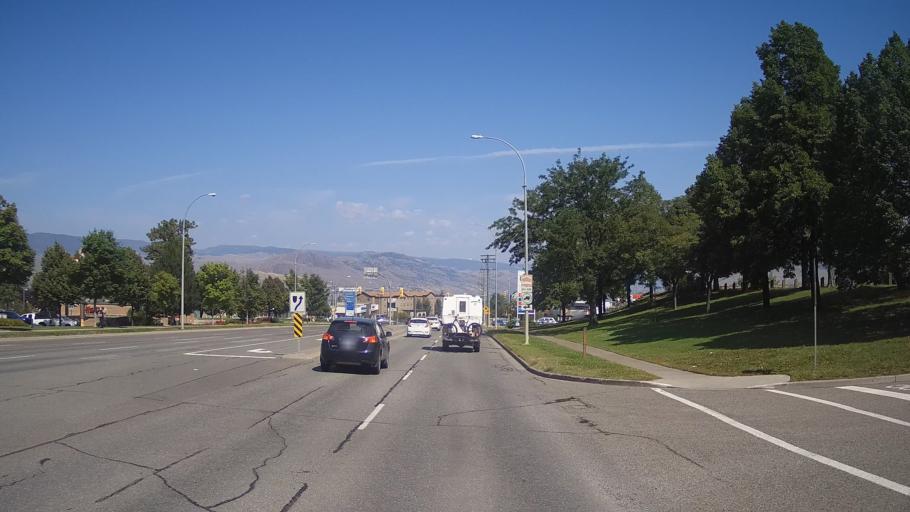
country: CA
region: British Columbia
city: Kamloops
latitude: 50.6683
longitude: -120.3543
